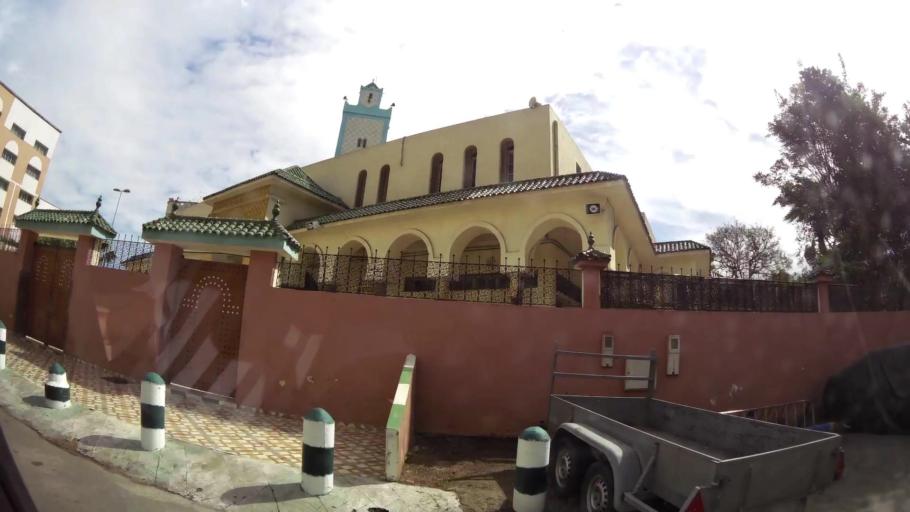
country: MA
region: Grand Casablanca
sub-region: Casablanca
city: Casablanca
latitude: 33.5783
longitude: -7.5848
